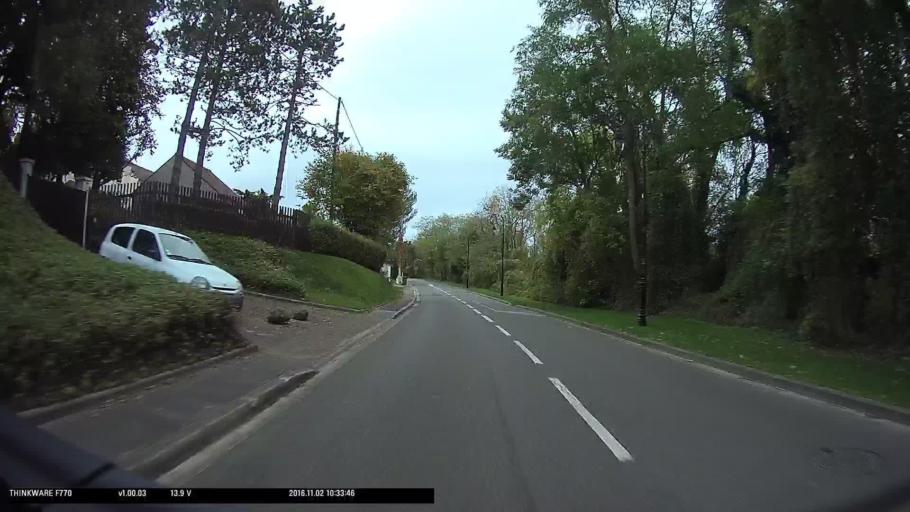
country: FR
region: Ile-de-France
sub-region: Departement du Val-d'Oise
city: Ableiges
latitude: 49.0887
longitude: 1.9886
